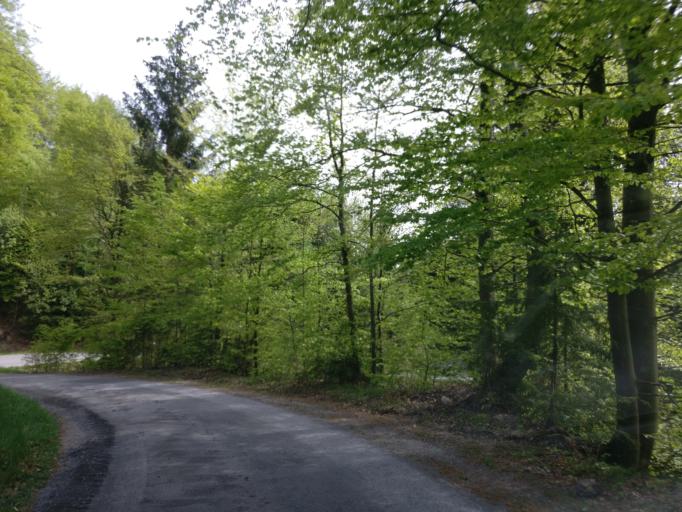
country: AT
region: Salzburg
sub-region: Politischer Bezirk Sankt Johann im Pongau
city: Werfen
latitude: 47.4751
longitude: 13.1989
